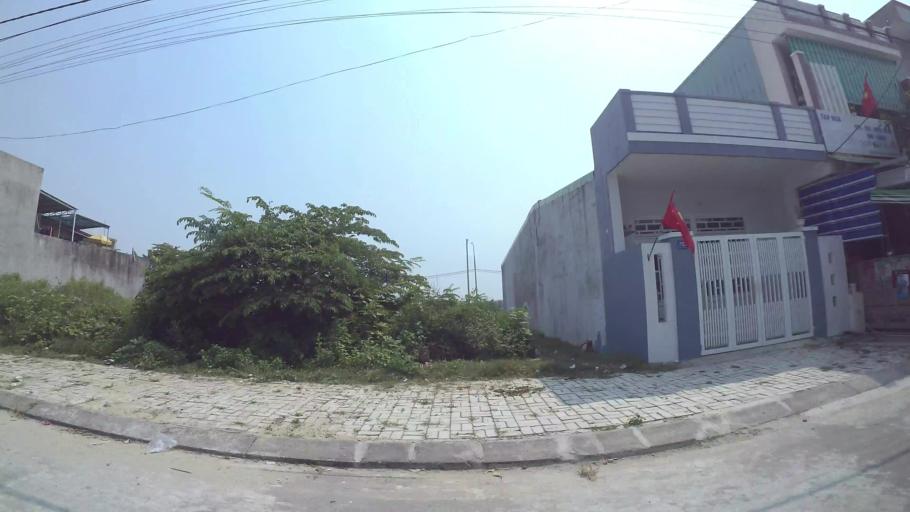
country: VN
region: Da Nang
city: Cam Le
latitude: 15.9837
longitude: 108.2163
